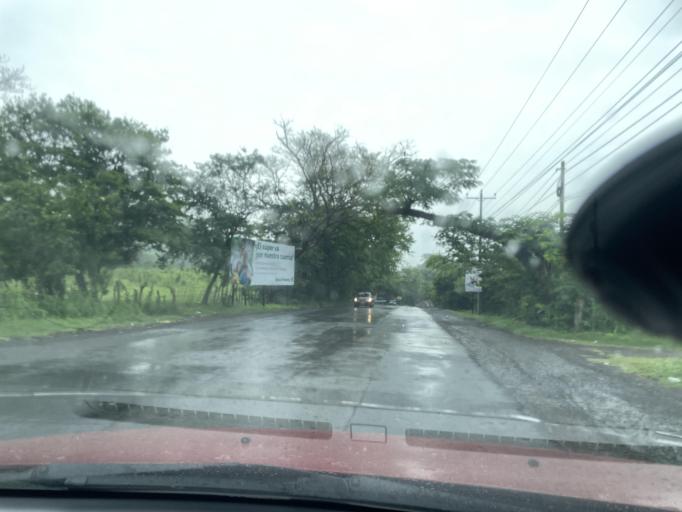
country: SV
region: La Union
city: Santa Rosa de Lima
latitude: 13.6069
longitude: -87.9106
